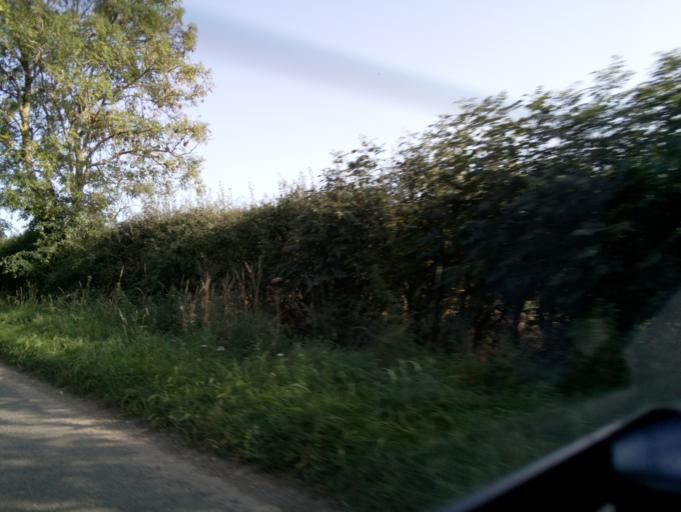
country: GB
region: England
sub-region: Gloucestershire
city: Gloucester
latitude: 51.9612
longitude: -2.2609
